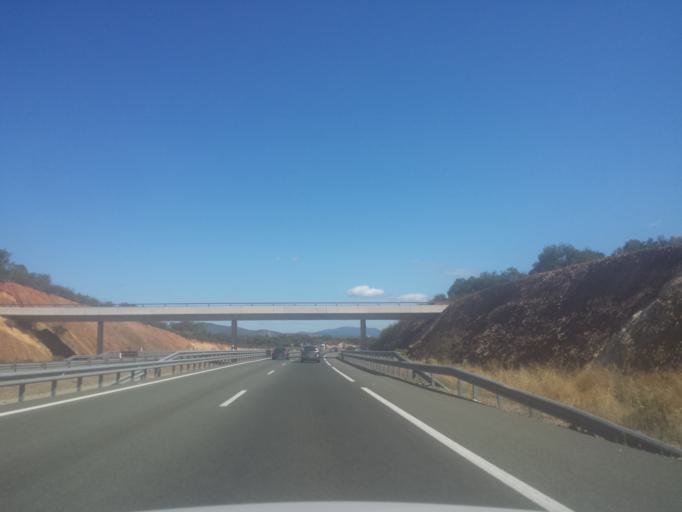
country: ES
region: Andalusia
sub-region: Provincia de Huelva
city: Santa Olalla del Cala
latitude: 37.8323
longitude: -6.2192
